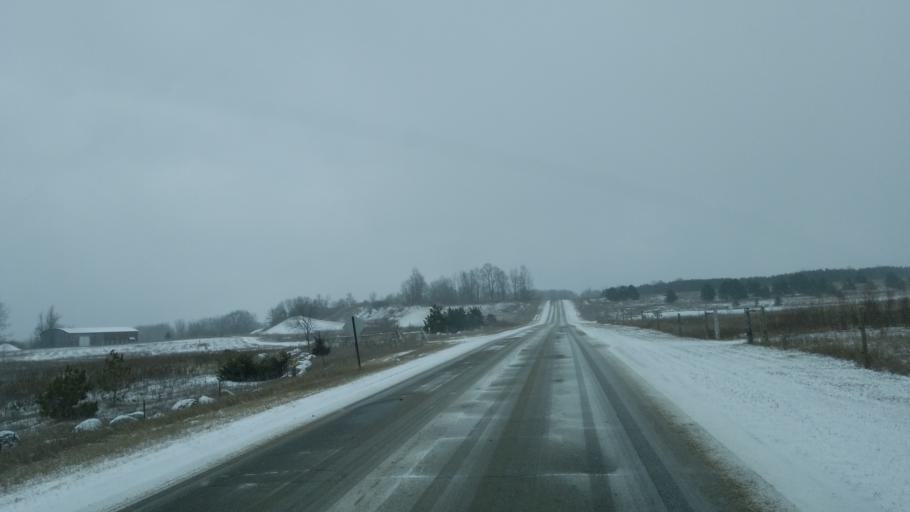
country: US
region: Michigan
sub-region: Osceola County
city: Reed City
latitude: 43.8493
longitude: -85.4227
